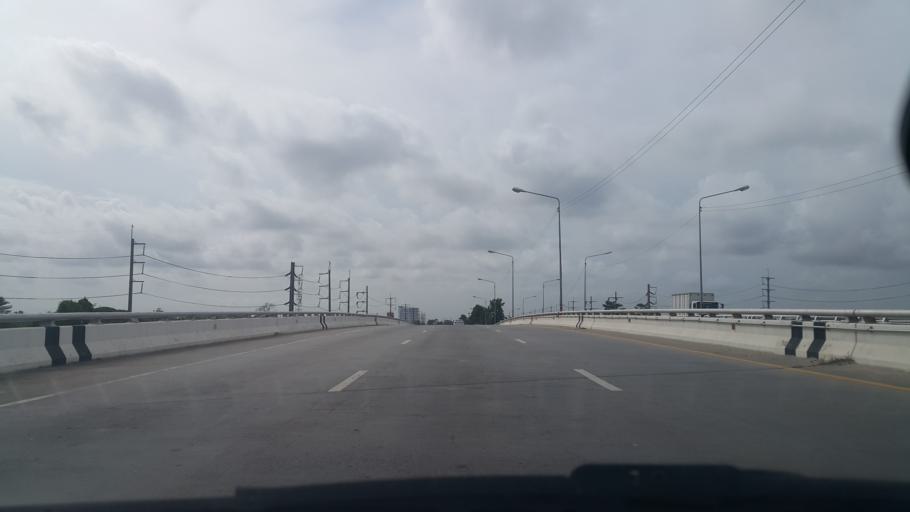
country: TH
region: Rayong
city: Rayong
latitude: 12.6831
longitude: 101.2996
